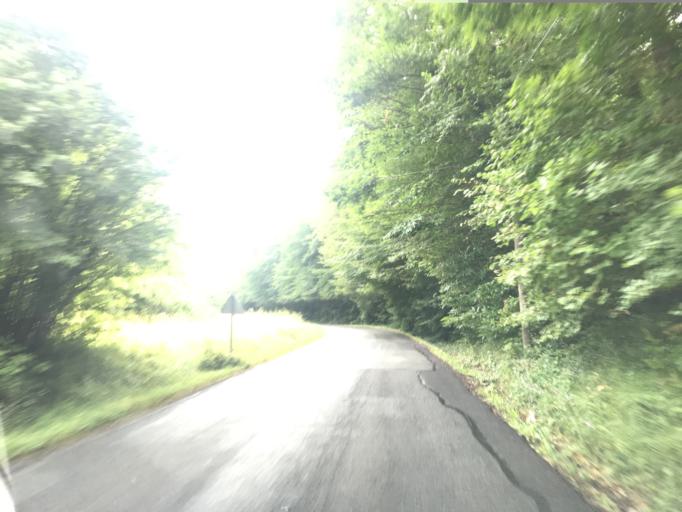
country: FR
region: Aquitaine
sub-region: Departement de la Dordogne
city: Chancelade
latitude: 45.1769
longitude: 0.6749
